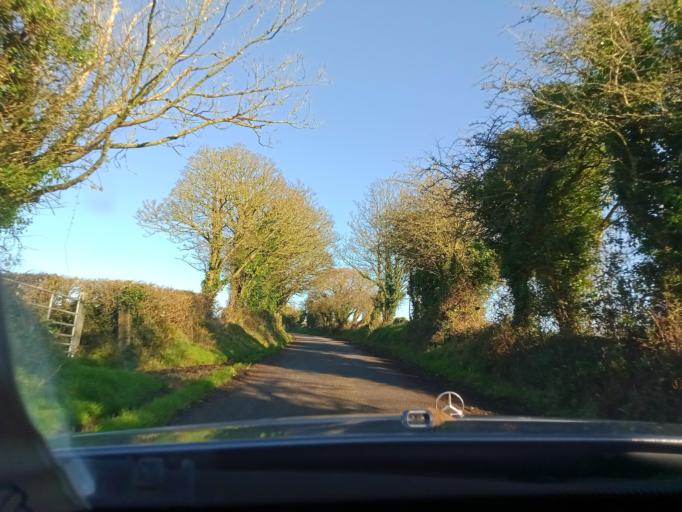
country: IE
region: Leinster
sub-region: Kilkenny
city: Mooncoin
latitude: 52.3392
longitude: -7.2561
